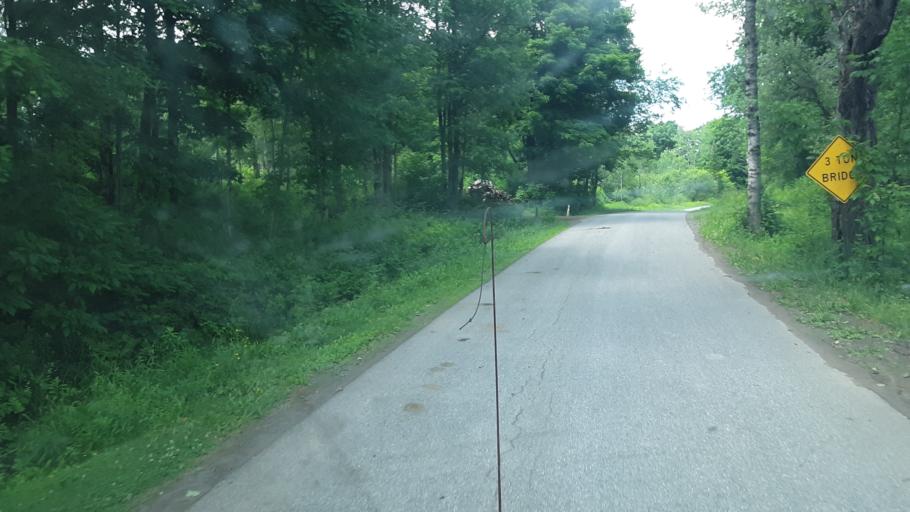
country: US
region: New York
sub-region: Oneida County
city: Rome
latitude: 43.3640
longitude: -75.4779
